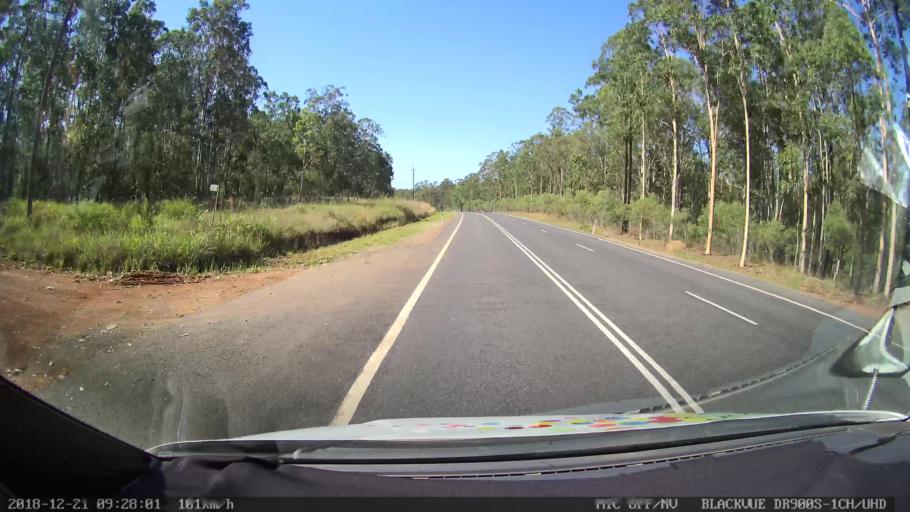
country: AU
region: New South Wales
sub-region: Clarence Valley
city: Maclean
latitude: -29.4111
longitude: 152.9873
